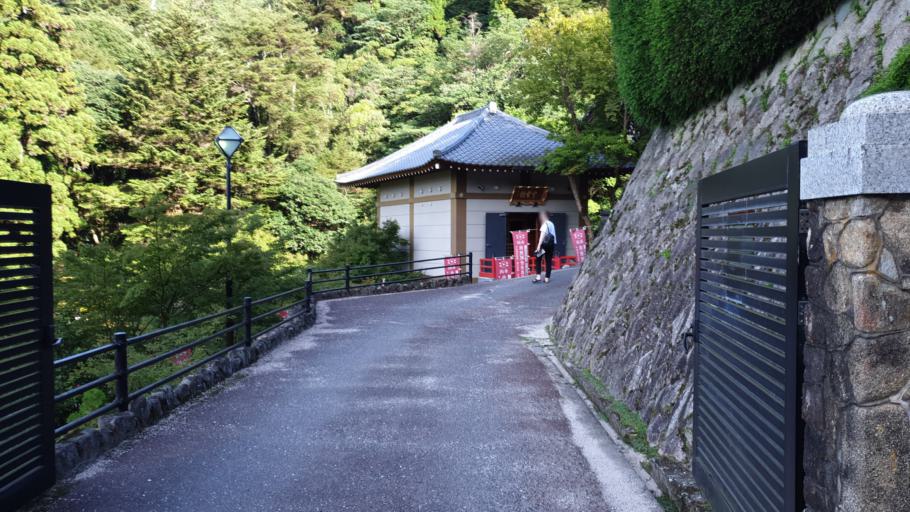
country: JP
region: Hiroshima
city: Miyajima
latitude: 34.2924
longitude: 132.3186
